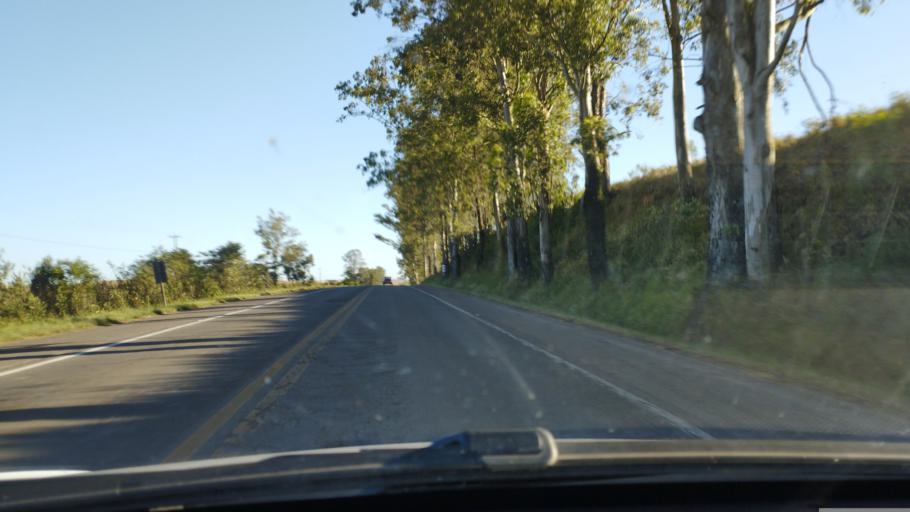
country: BR
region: Rio Grande do Sul
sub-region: Julio De Castilhos
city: Julio de Castilhos
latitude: -29.4036
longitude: -53.6683
